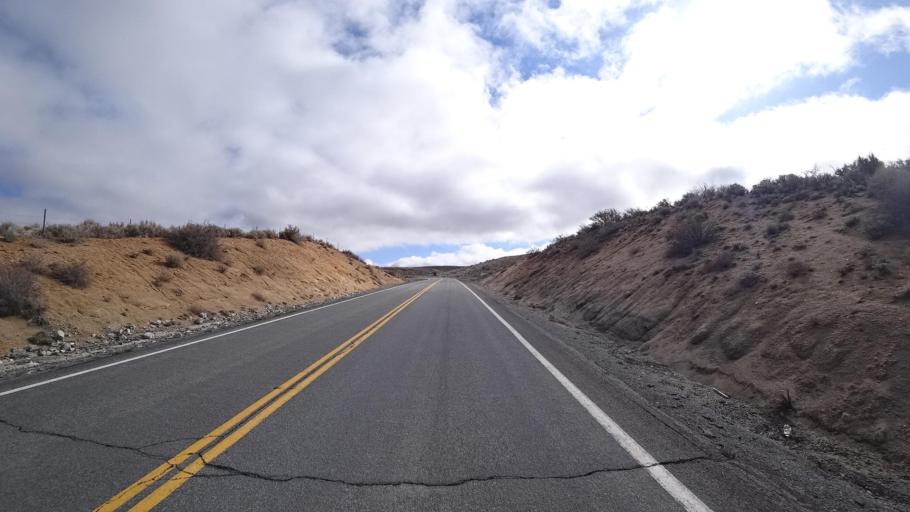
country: US
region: Nevada
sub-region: Washoe County
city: Cold Springs
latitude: 39.8036
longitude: -119.9292
